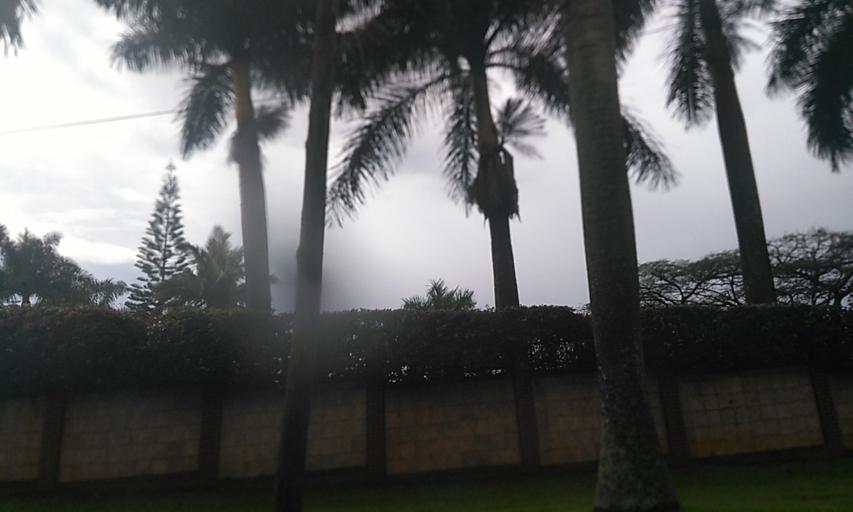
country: UG
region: Central Region
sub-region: Kampala District
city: Kampala
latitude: 0.3288
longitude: 32.5890
